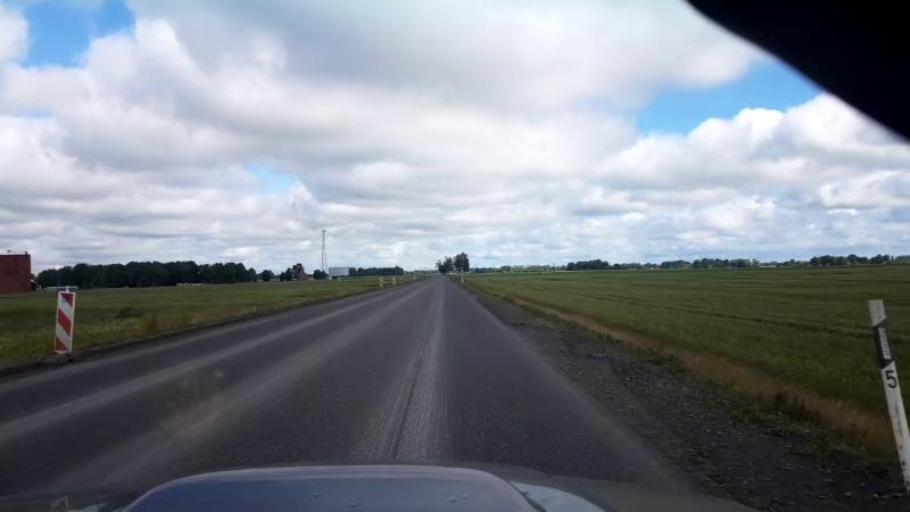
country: LV
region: Bauskas Rajons
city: Bauska
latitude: 56.2860
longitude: 24.3580
